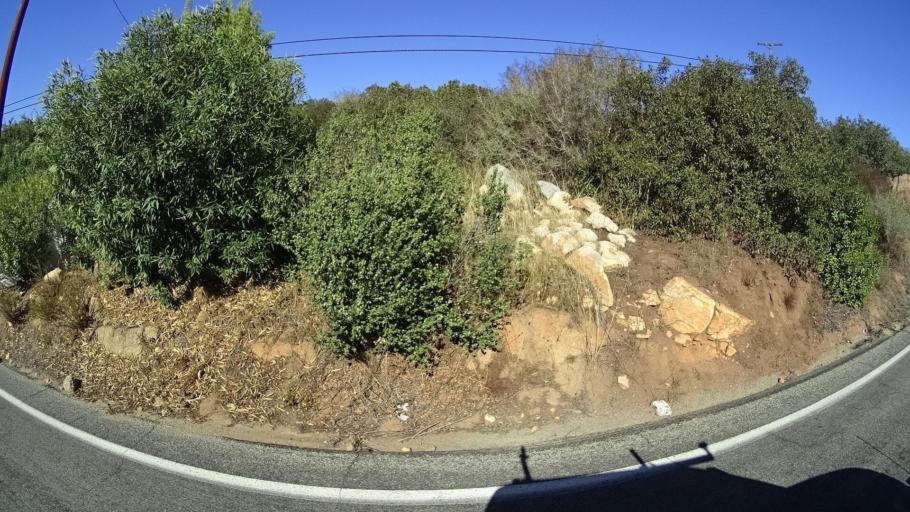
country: US
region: California
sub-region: San Diego County
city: Jamul
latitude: 32.7015
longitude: -116.7456
